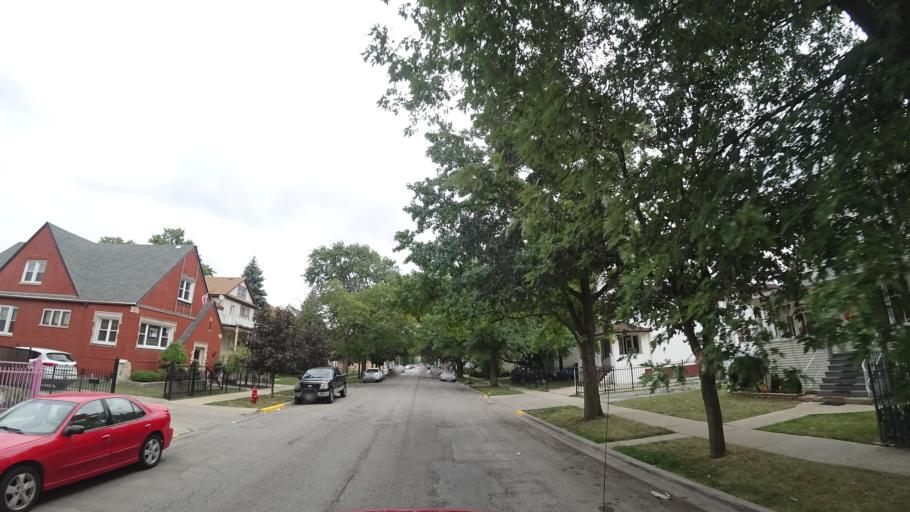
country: US
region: Illinois
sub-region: Cook County
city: Cicero
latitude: 41.8474
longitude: -87.7555
